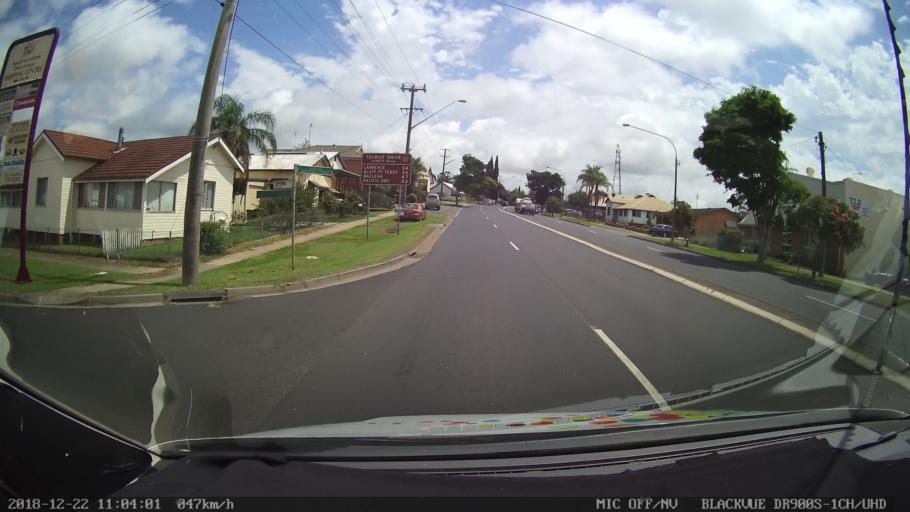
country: AU
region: New South Wales
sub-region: Clarence Valley
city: South Grafton
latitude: -29.7054
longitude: 152.9398
